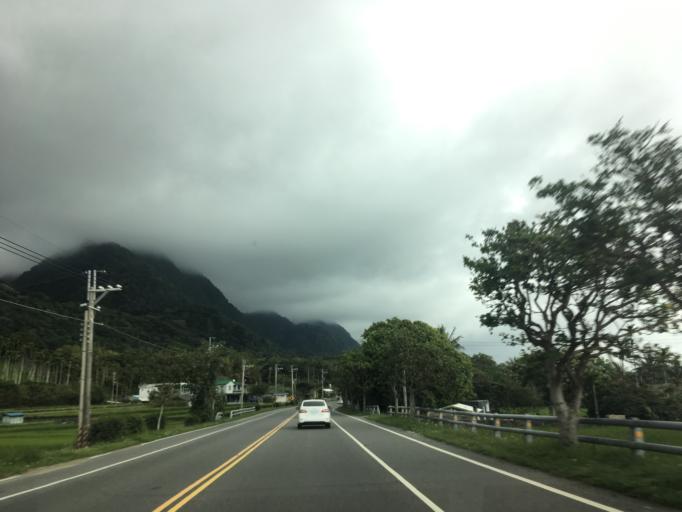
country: TW
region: Taiwan
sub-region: Taitung
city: Taitung
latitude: 23.0105
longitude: 121.3238
